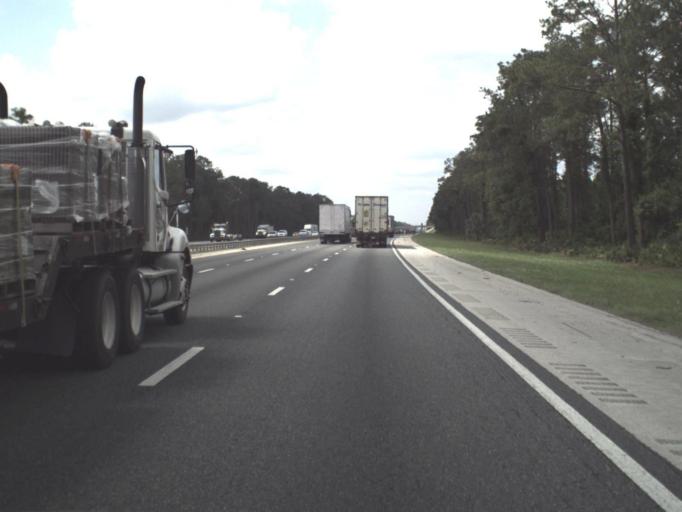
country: US
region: Florida
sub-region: Saint Johns County
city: Saint Augustine South
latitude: 29.8517
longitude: -81.3918
